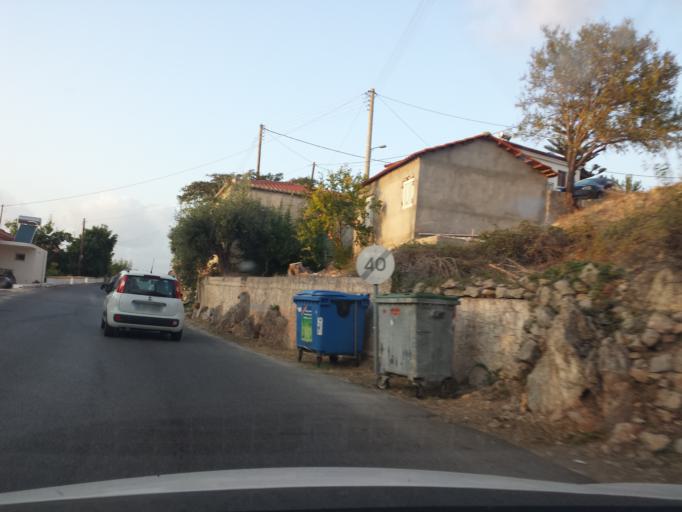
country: GR
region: Peloponnese
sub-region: Nomos Messinias
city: Pylos
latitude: 36.9175
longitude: 21.7018
